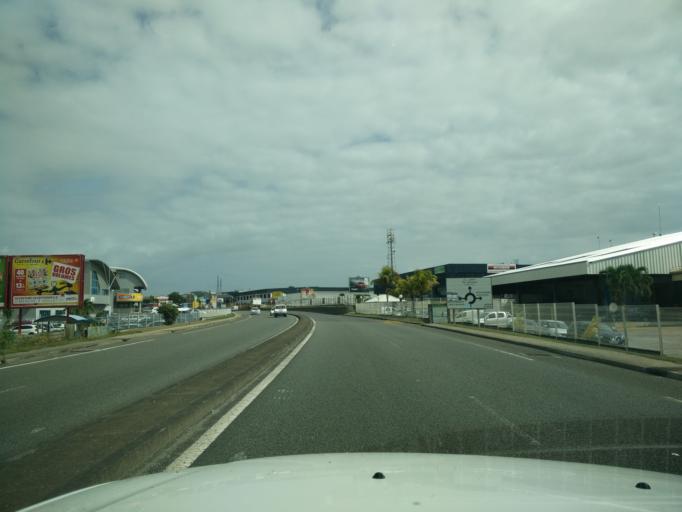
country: GP
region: Guadeloupe
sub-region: Guadeloupe
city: Baie-Mahault
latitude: 16.2436
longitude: -61.5719
